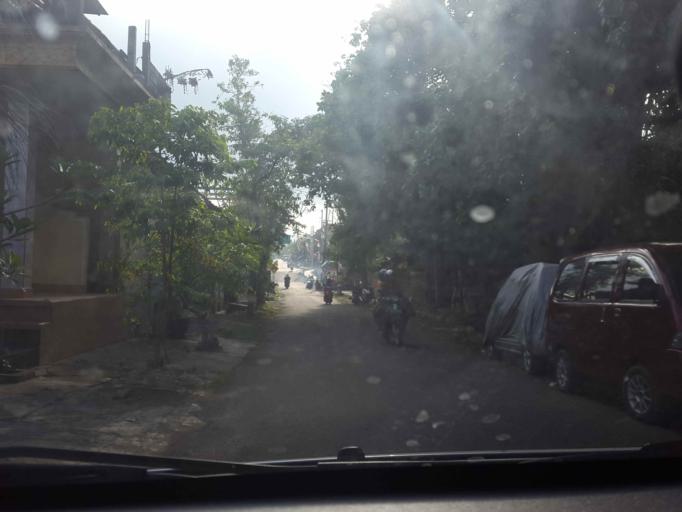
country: ID
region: Bali
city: Semarapura
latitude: -8.5370
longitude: 115.4163
